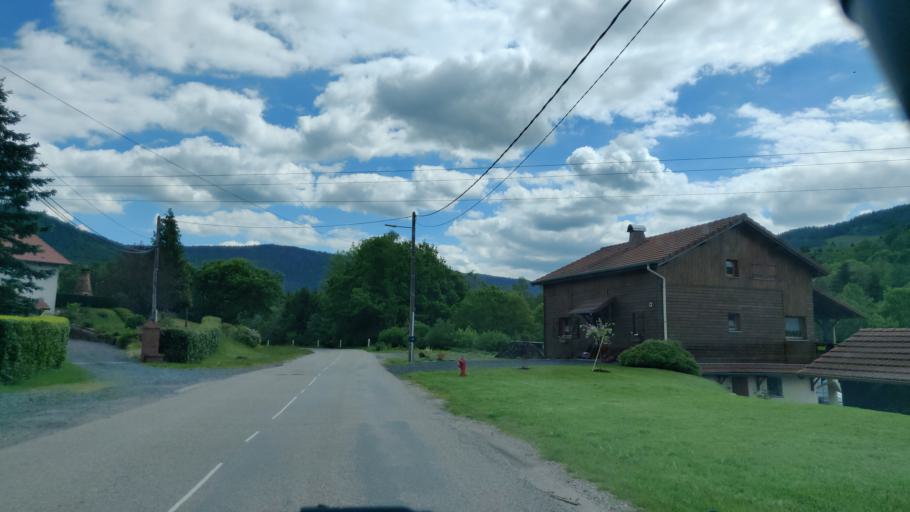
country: FR
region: Lorraine
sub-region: Departement des Vosges
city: Fraize
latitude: 48.1665
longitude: 6.9813
